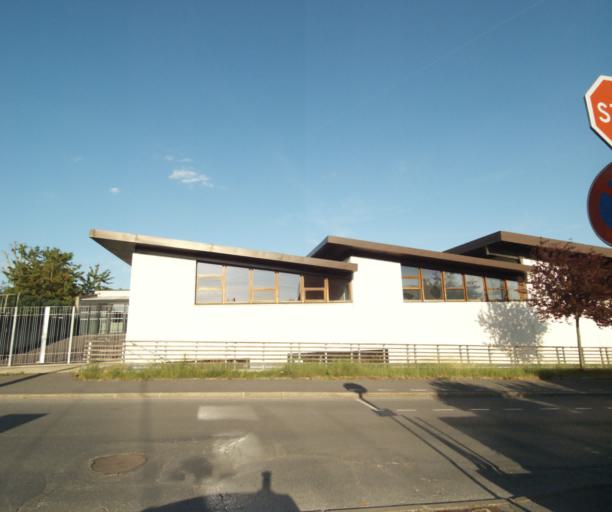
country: FR
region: Champagne-Ardenne
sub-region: Departement des Ardennes
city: Charleville-Mezieres
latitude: 49.7859
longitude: 4.7097
